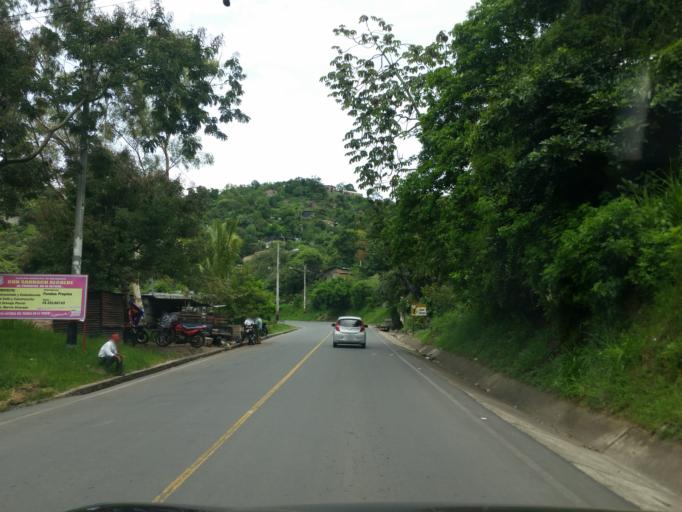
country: NI
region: Matagalpa
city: Matagalpa
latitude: 12.9393
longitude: -85.9206
